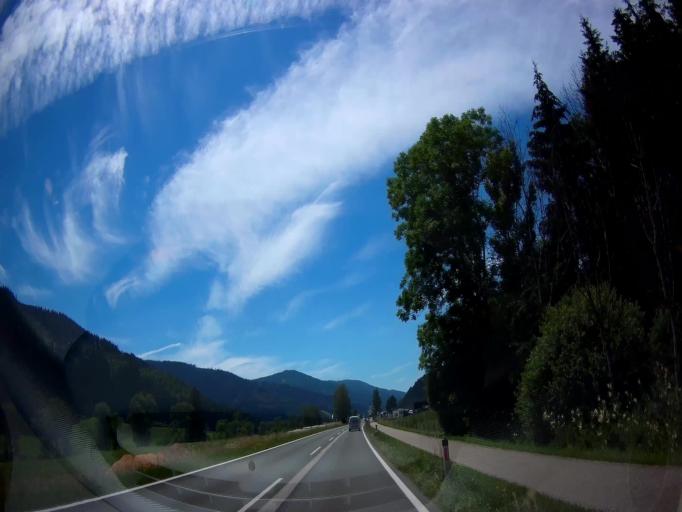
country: AT
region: Carinthia
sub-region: Politischer Bezirk Sankt Veit an der Glan
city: Strassburg
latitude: 46.8844
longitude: 14.3117
